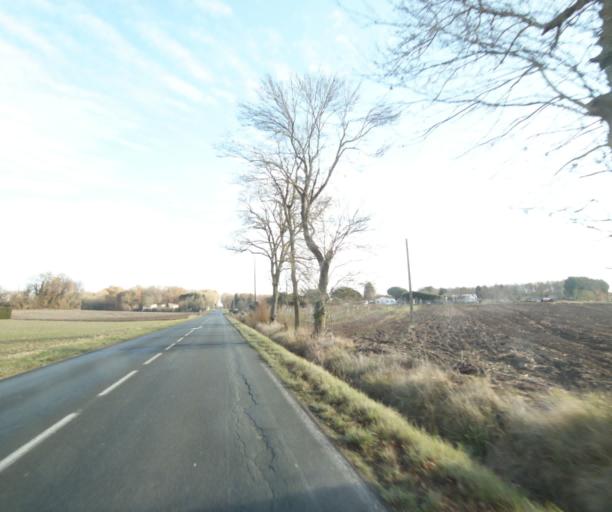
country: FR
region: Poitou-Charentes
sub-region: Departement de la Charente-Maritime
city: Nieul-les-Saintes
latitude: 45.7323
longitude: -0.7141
